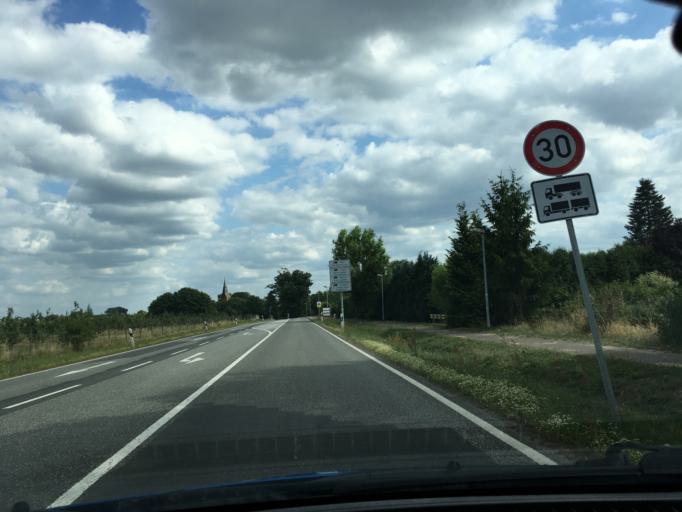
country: DE
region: Mecklenburg-Vorpommern
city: Lubtheen
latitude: 53.3818
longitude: 11.0738
